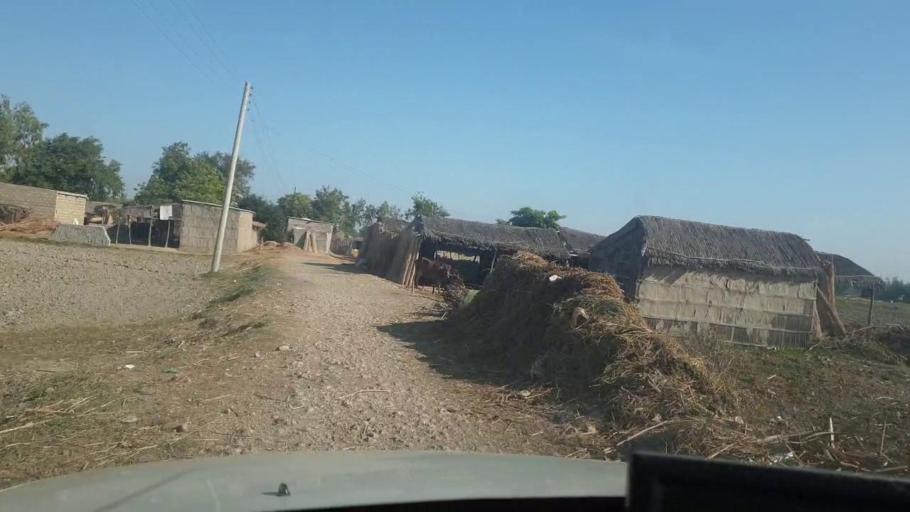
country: PK
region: Sindh
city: Mirpur Sakro
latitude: 24.4952
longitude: 67.6326
